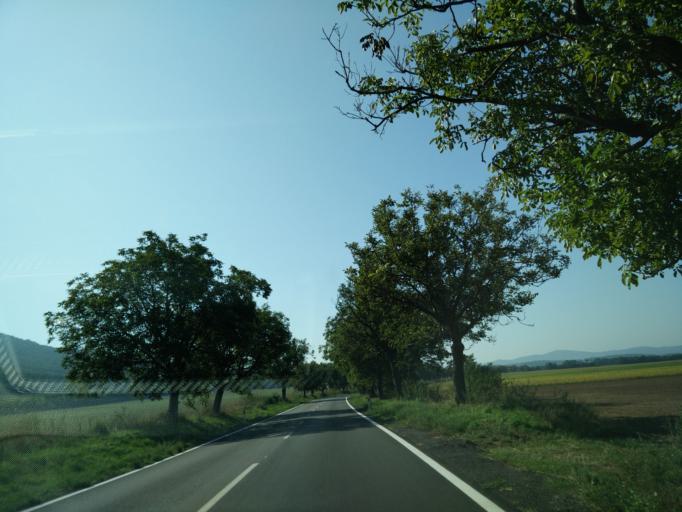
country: SK
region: Nitriansky
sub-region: Okres Nitra
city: Nitra
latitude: 48.4560
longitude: 18.1430
